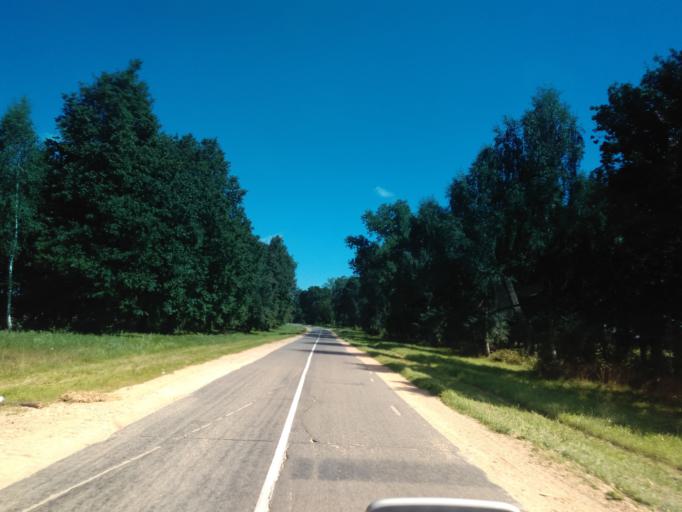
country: BY
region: Minsk
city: Stan'kava
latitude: 53.6284
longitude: 27.2652
